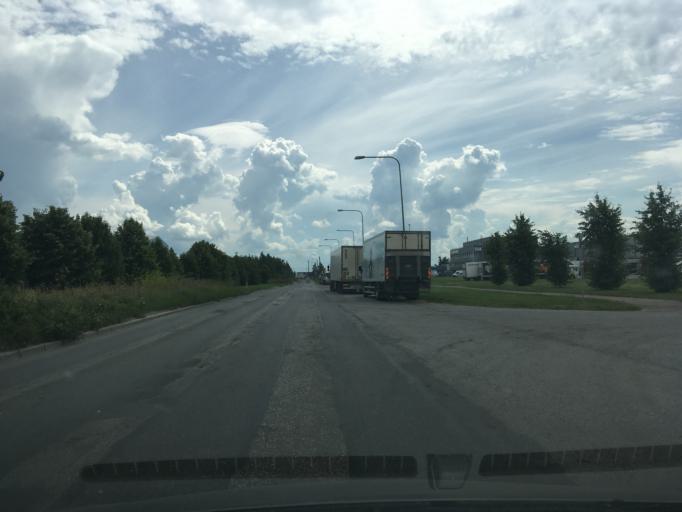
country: EE
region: Harju
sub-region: Tallinna linn
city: Kose
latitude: 59.4283
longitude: 24.8494
